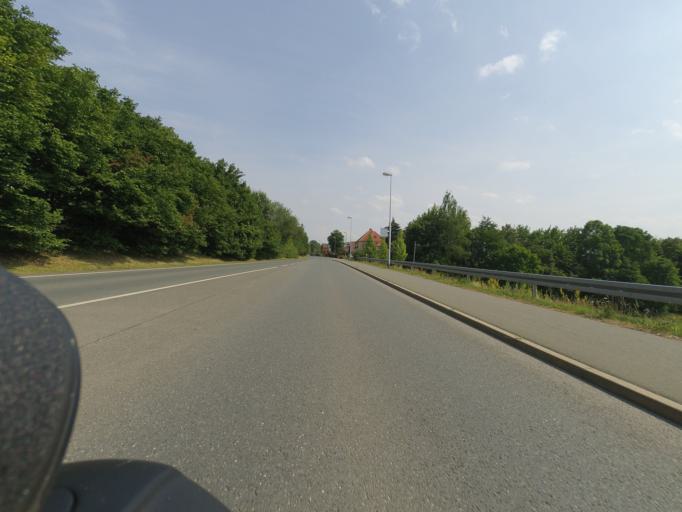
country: DE
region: Thuringia
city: Bad Kostritz
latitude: 50.9242
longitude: 12.0433
